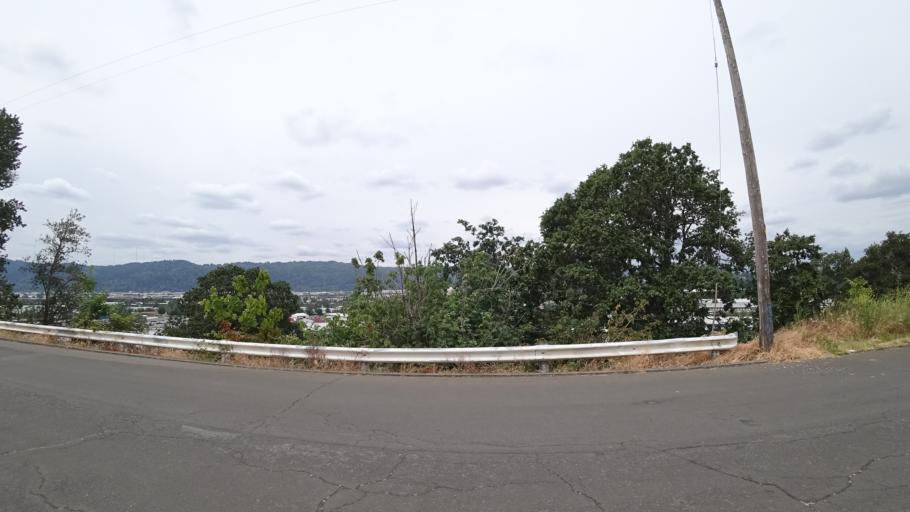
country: US
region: Oregon
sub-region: Multnomah County
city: Portland
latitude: 45.5677
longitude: -122.6994
